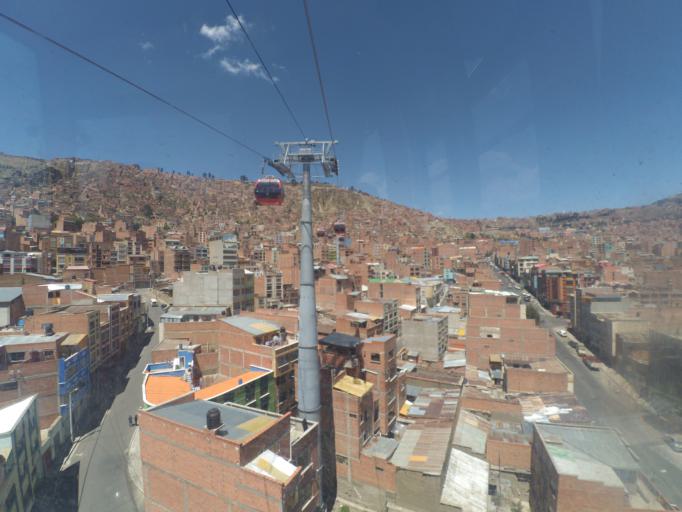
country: BO
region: La Paz
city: La Paz
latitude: -16.4981
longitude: -68.1553
